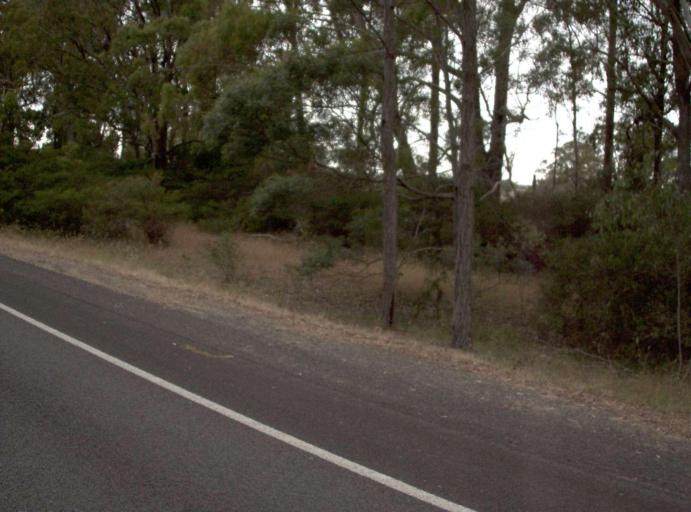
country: AU
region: Victoria
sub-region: Wellington
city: Sale
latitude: -38.4448
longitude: 146.9440
